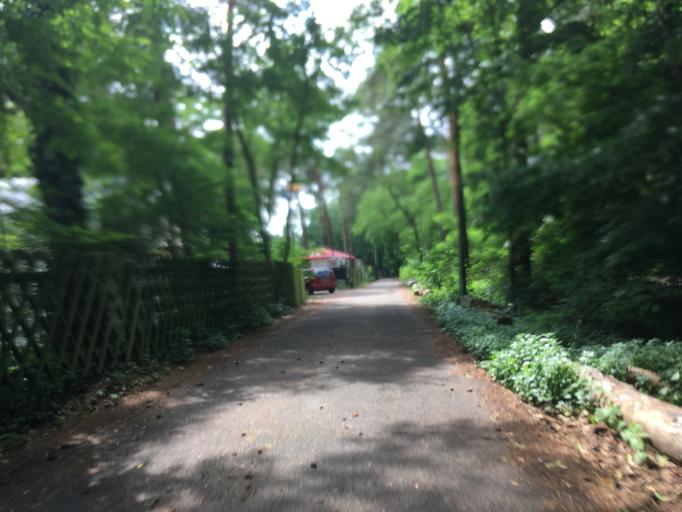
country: DE
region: Berlin
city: Schmockwitz
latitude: 52.3905
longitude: 13.6514
